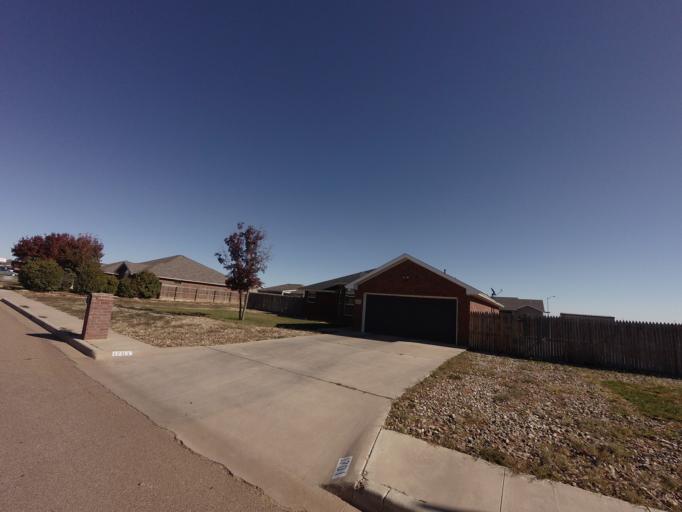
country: US
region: New Mexico
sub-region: Curry County
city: Clovis
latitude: 34.4131
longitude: -103.1665
